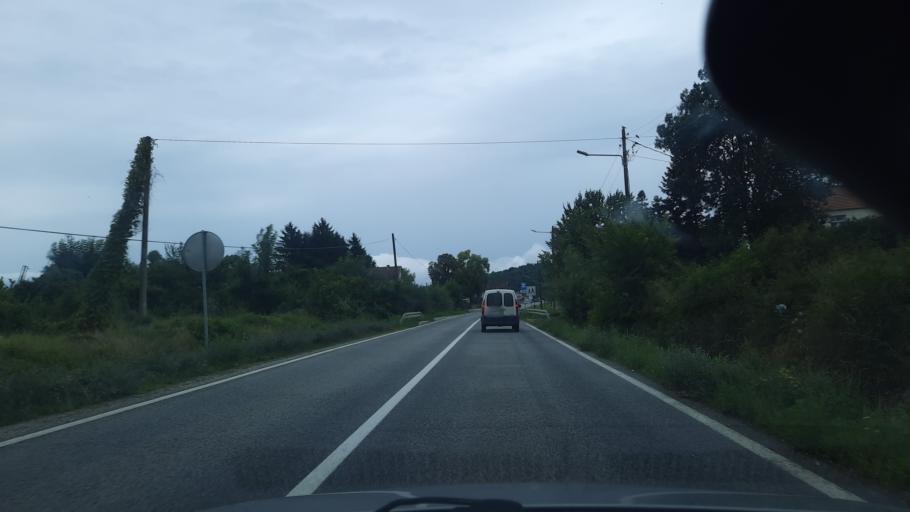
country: RS
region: Central Serbia
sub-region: Raski Okrug
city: Kraljevo
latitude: 43.7287
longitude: 20.8023
